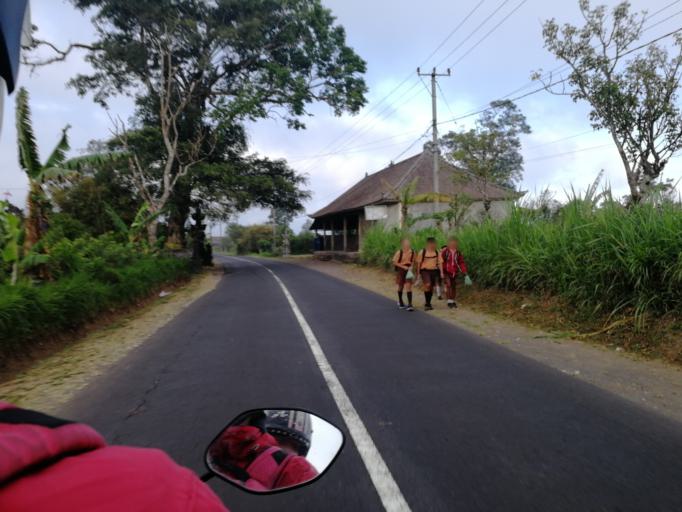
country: ID
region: Bali
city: Banjar Kedisan
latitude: -8.2217
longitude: 115.2676
